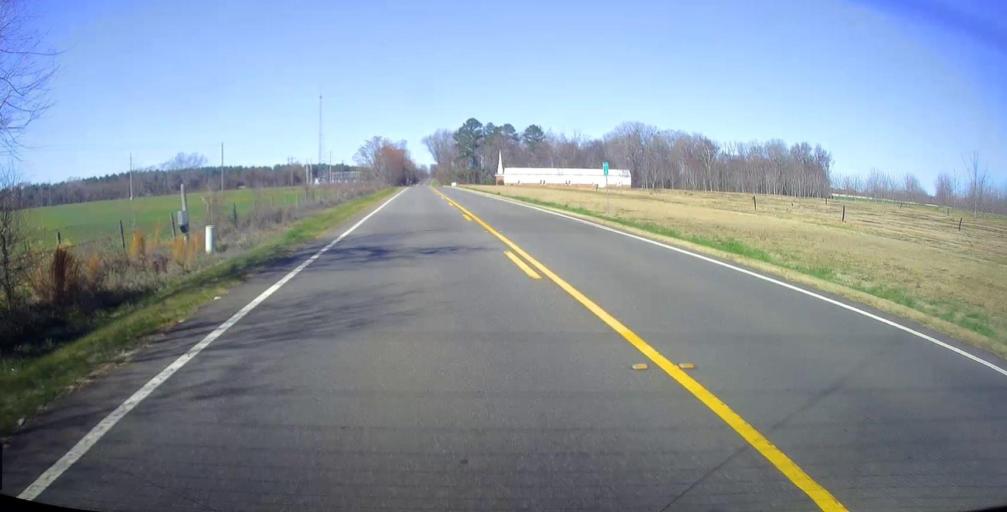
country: US
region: Georgia
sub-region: Macon County
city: Montezuma
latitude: 32.3721
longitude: -84.0139
